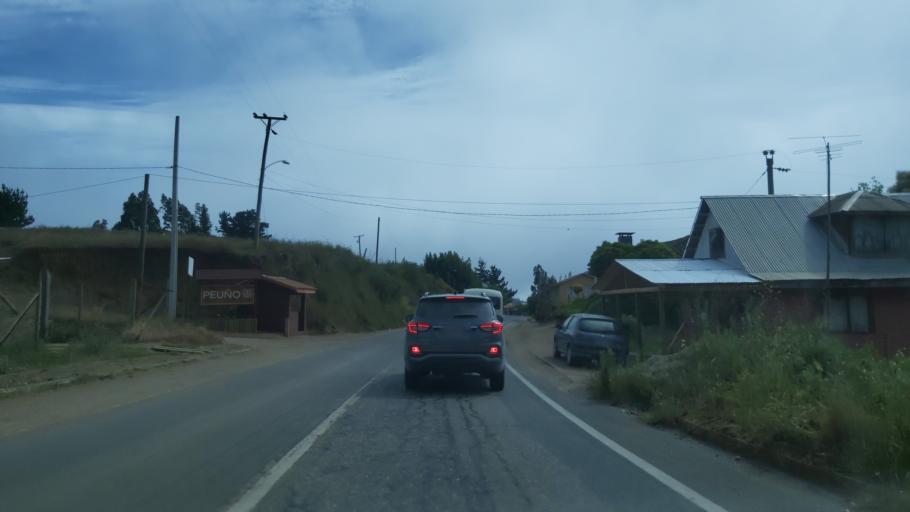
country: CL
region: Maule
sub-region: Provincia de Cauquenes
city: Cauquenes
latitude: -35.8701
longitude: -72.6559
